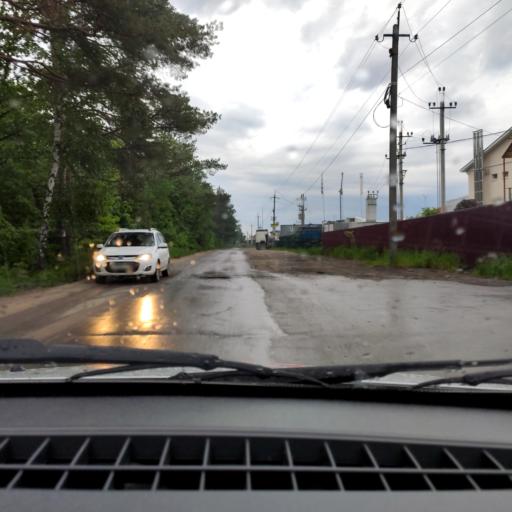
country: RU
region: Voronezj
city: Ramon'
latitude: 51.8478
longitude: 39.2212
